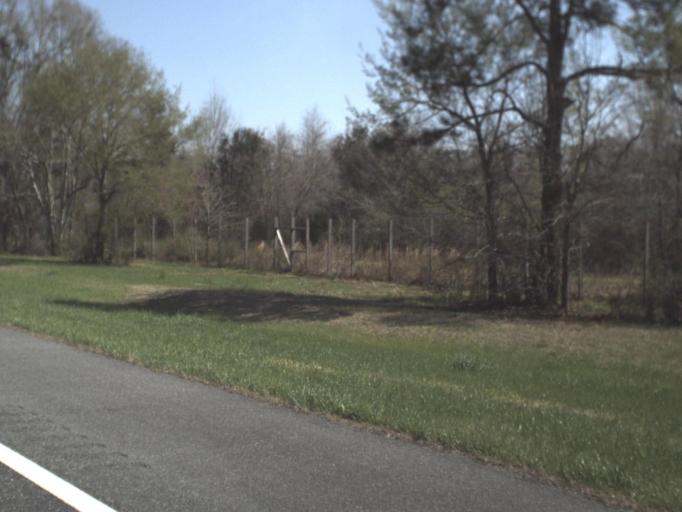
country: US
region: Florida
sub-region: Washington County
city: Chipley
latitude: 30.7469
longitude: -85.4249
